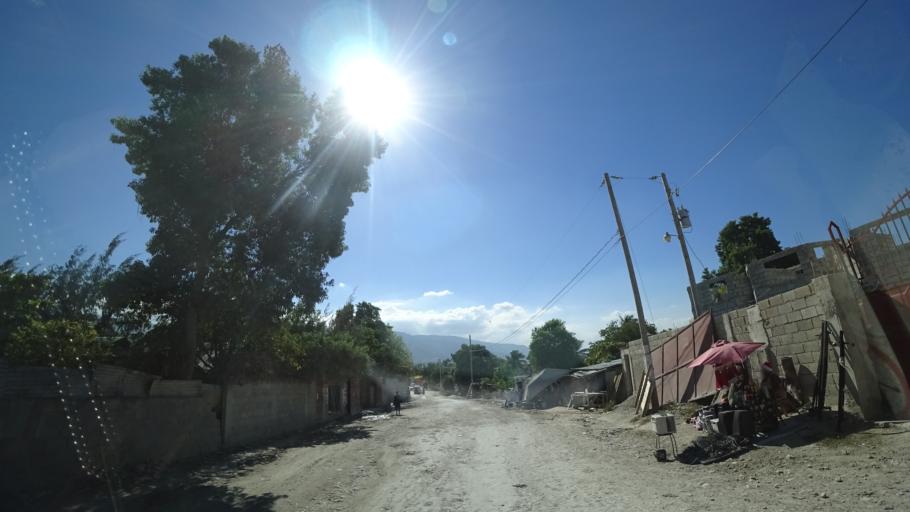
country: HT
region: Ouest
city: Delmas 73
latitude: 18.5552
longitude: -72.2839
